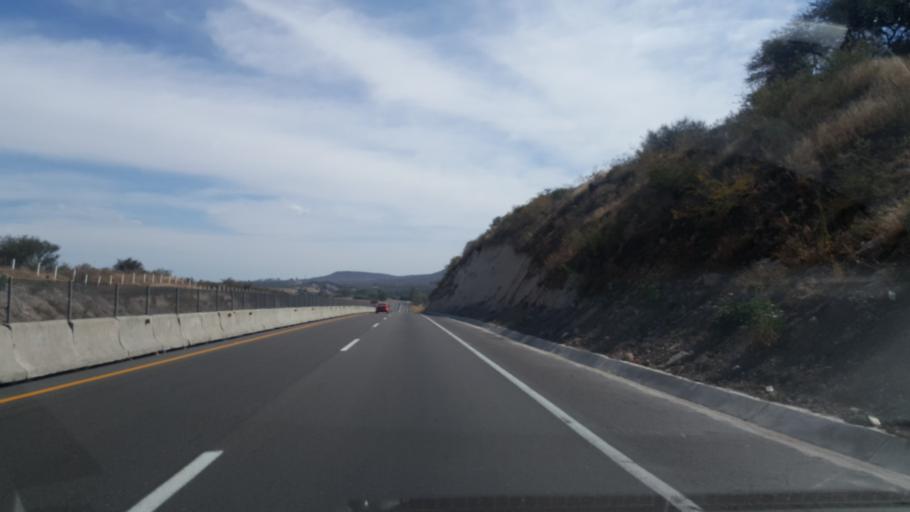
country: MX
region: Jalisco
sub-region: Lagos de Moreno
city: Cristeros [Fraccionamiento]
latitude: 21.2897
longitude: -102.0058
